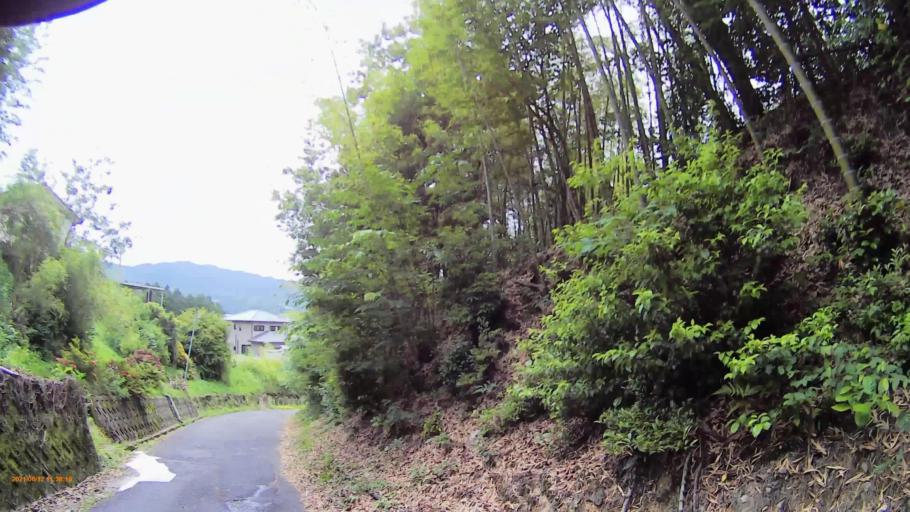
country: JP
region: Gifu
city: Nakatsugawa
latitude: 35.4734
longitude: 137.4520
